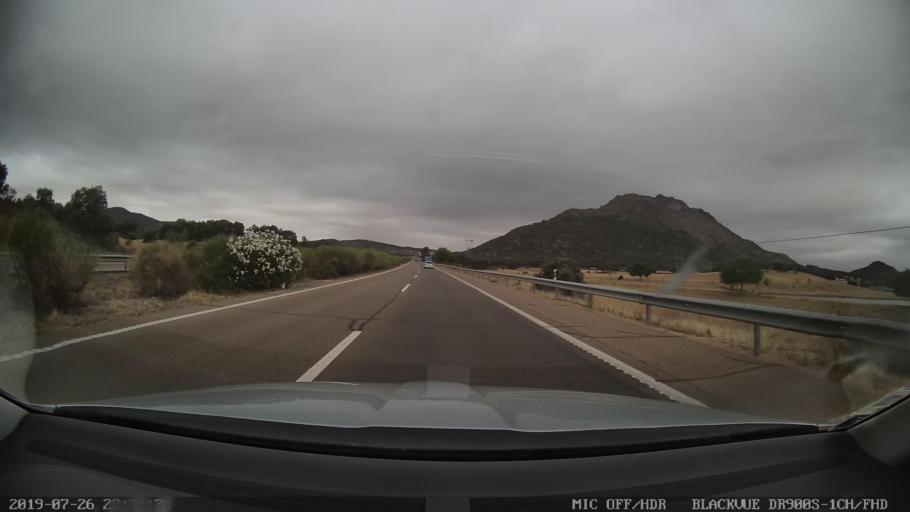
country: ES
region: Extremadura
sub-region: Provincia de Caceres
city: Puerto de Santa Cruz
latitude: 39.2967
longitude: -5.8554
